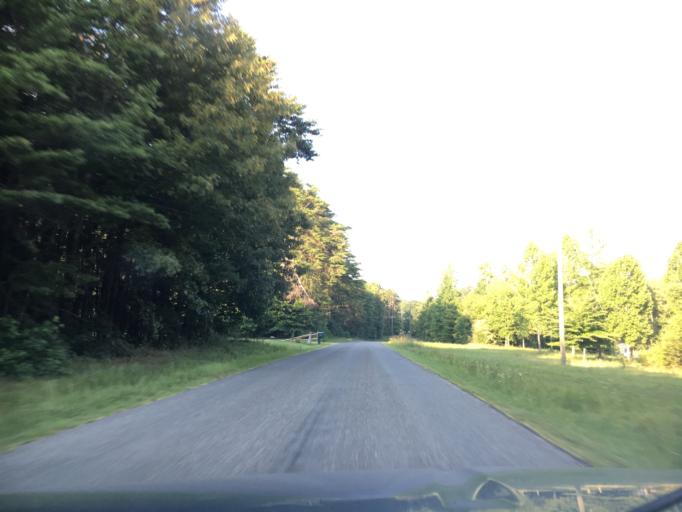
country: US
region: Virginia
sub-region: Pittsylvania County
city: Gretna
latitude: 36.8427
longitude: -79.1868
